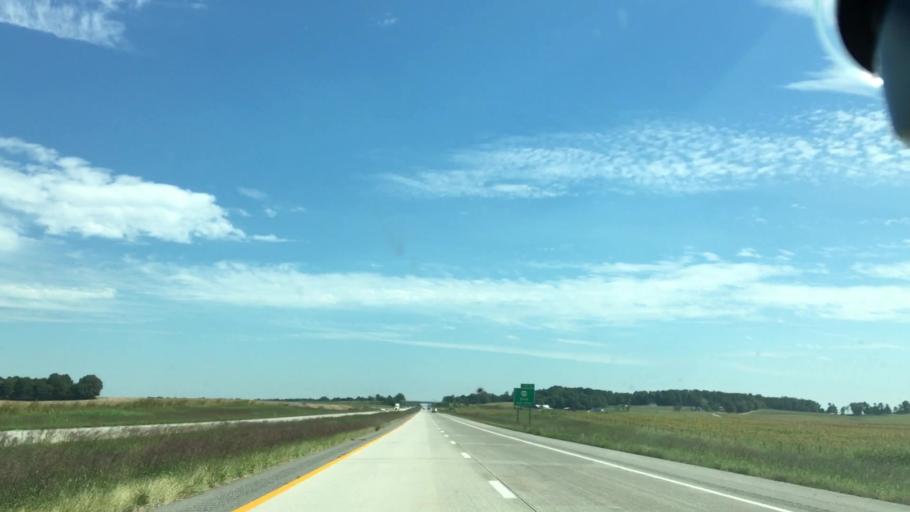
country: US
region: Kentucky
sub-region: Henderson County
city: Henderson
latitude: 37.7900
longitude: -87.4836
